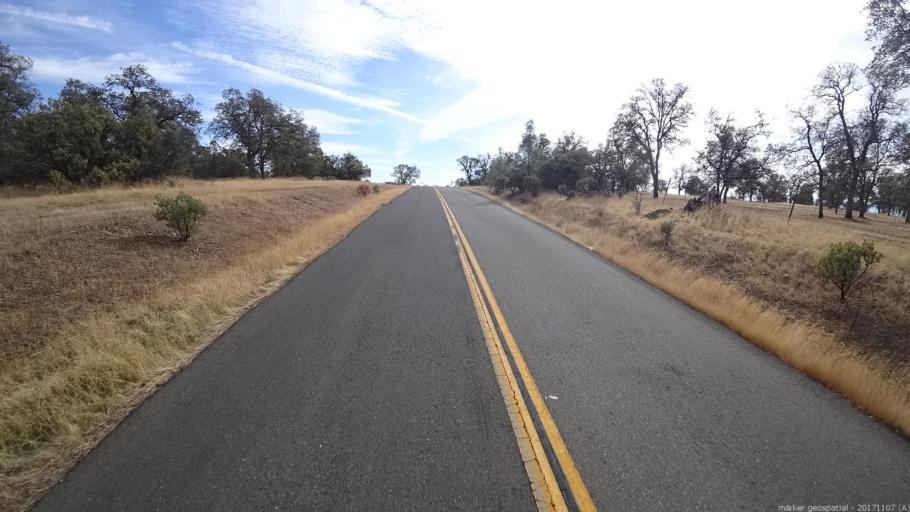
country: US
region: California
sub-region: Shasta County
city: Shasta
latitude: 40.4890
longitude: -122.5491
